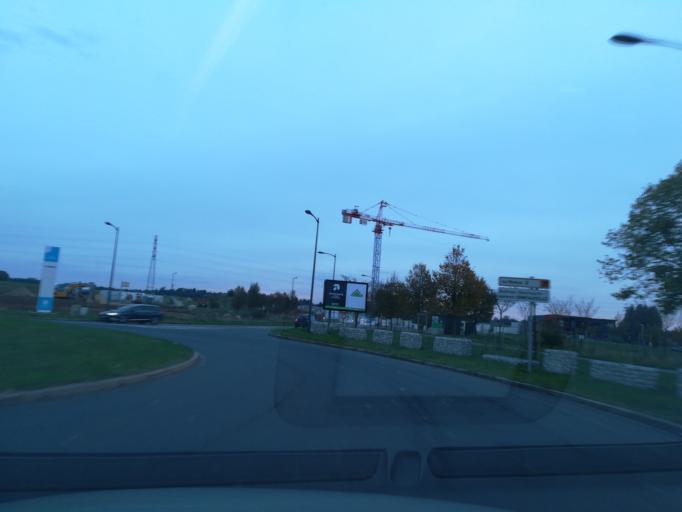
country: FR
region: Haute-Normandie
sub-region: Departement de la Seine-Maritime
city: Isneauville
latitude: 49.4886
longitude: 1.1470
